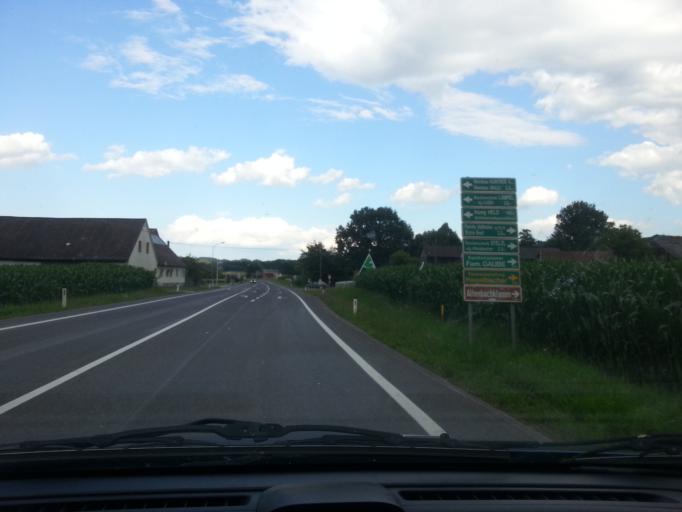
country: AT
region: Styria
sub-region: Politischer Bezirk Leibnitz
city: Oberhaag
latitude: 46.6853
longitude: 15.3509
